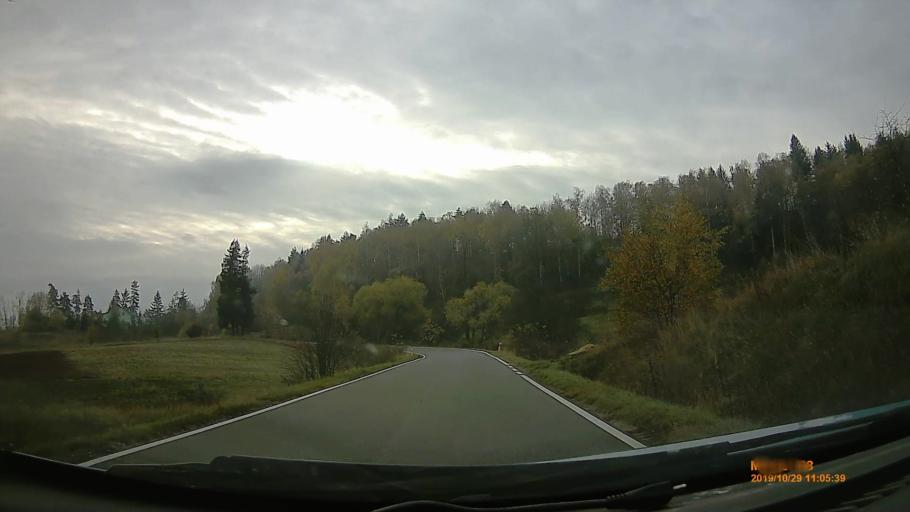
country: PL
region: Lower Silesian Voivodeship
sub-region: Powiat klodzki
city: Szczytna
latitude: 50.4686
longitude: 16.4765
